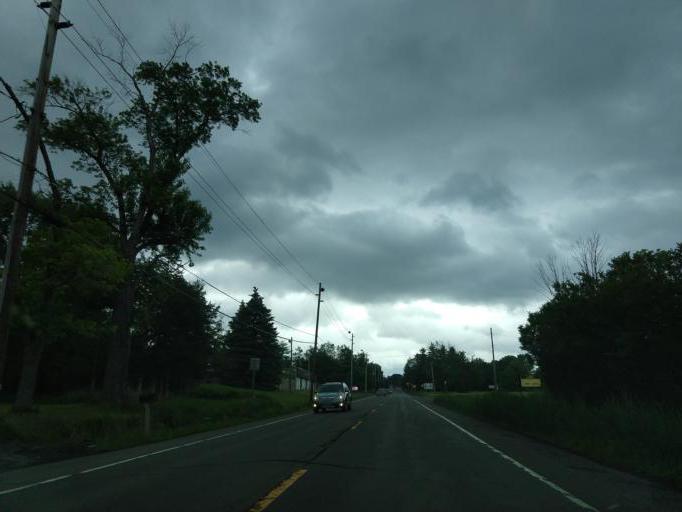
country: US
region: New York
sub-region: Tompkins County
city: Lansing
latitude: 42.5398
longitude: -76.5145
